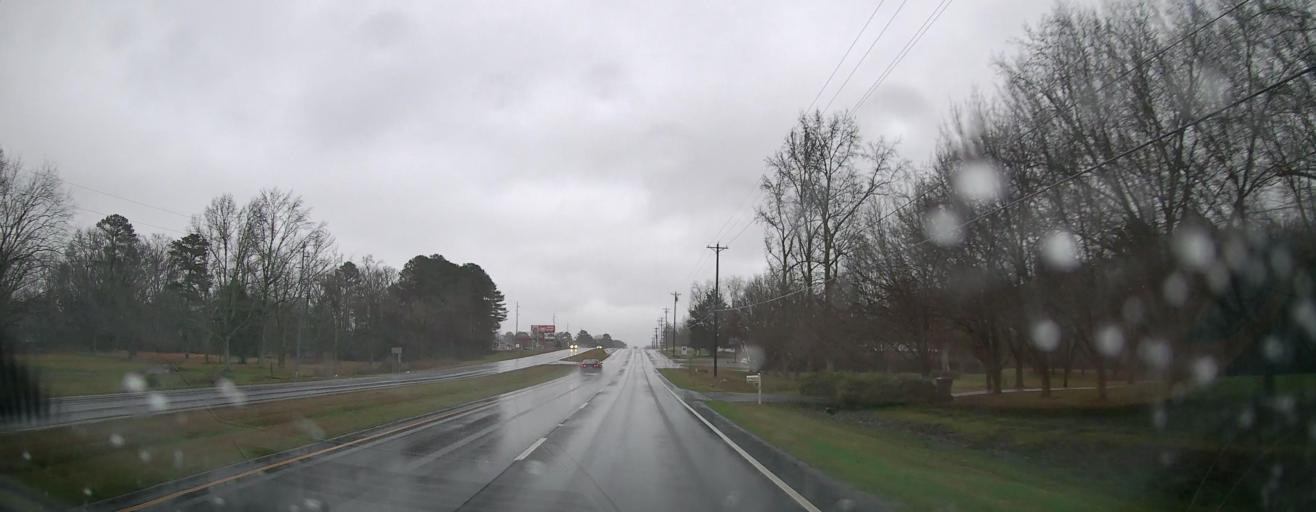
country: US
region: Alabama
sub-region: Morgan County
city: Hartselle
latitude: 34.4656
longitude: -86.9527
